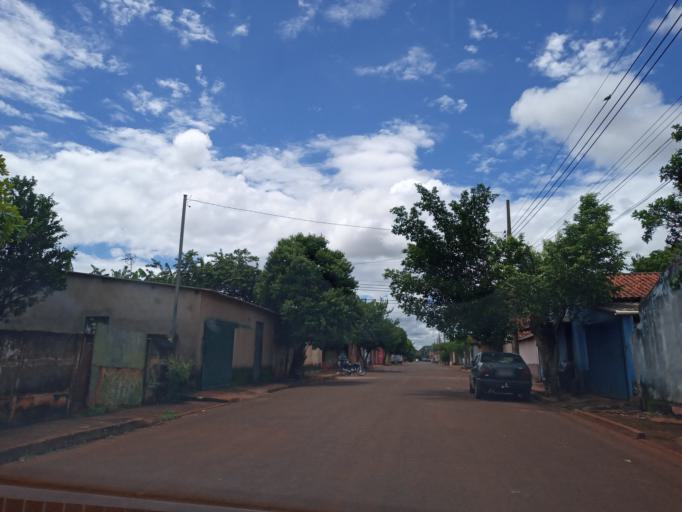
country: BR
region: Minas Gerais
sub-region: Centralina
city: Centralina
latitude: -18.5856
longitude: -49.2042
